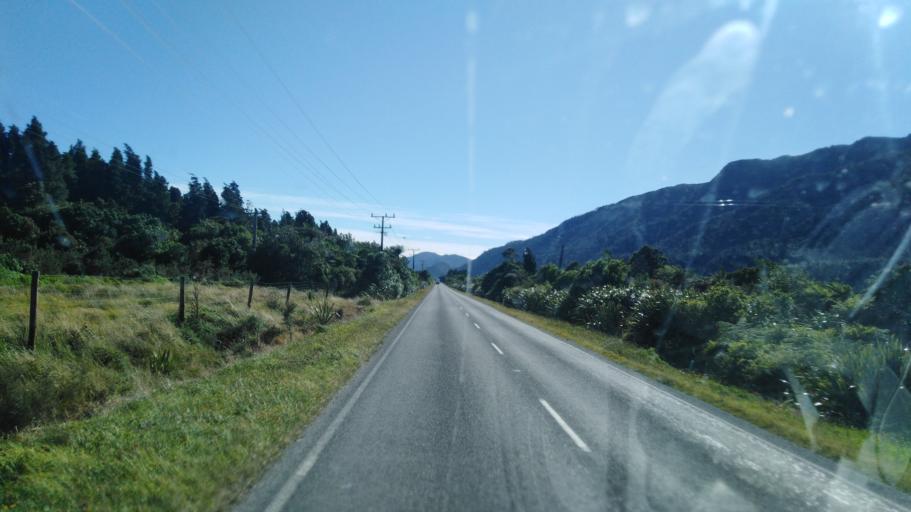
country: NZ
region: West Coast
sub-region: Buller District
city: Westport
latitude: -41.6624
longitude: 171.8152
